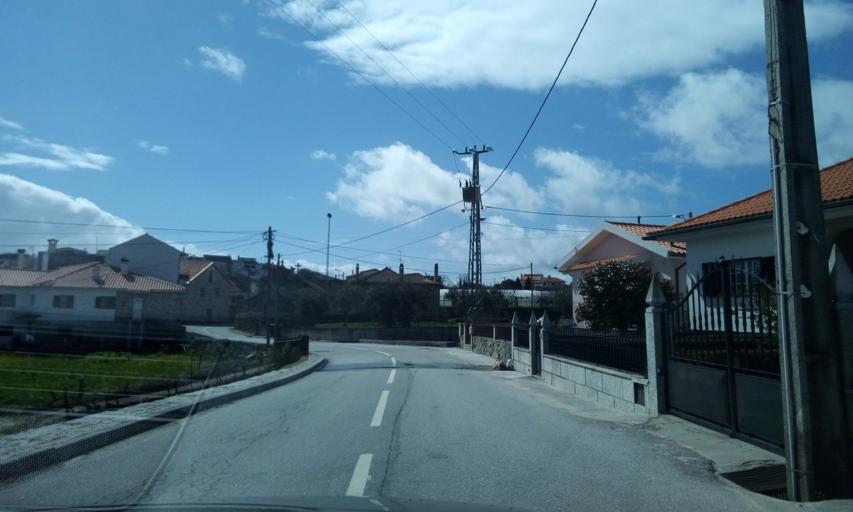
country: PT
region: Guarda
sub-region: Fornos de Algodres
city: Fornos de Algodres
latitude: 40.6312
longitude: -7.5371
